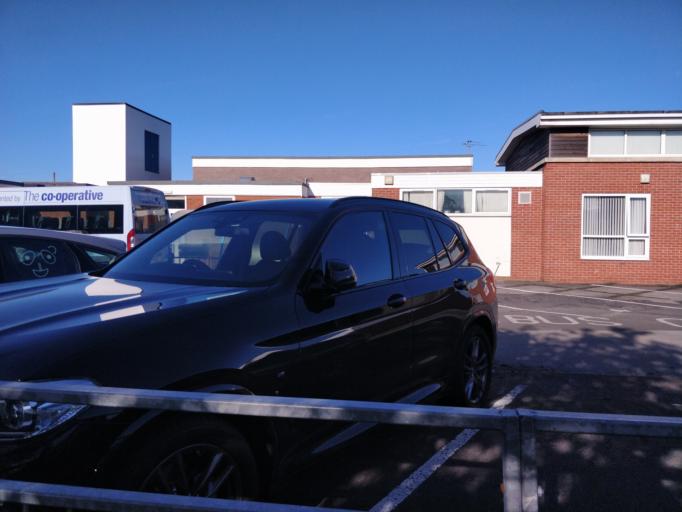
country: GB
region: England
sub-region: Sefton
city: Southport
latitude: 53.6662
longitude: -2.9630
